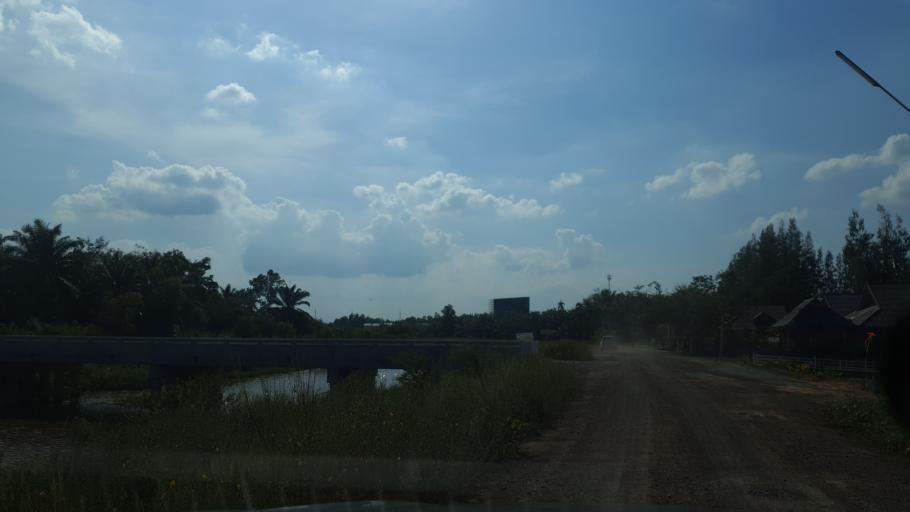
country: TH
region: Surat Thani
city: Phunphin
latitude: 9.1450
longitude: 99.1618
